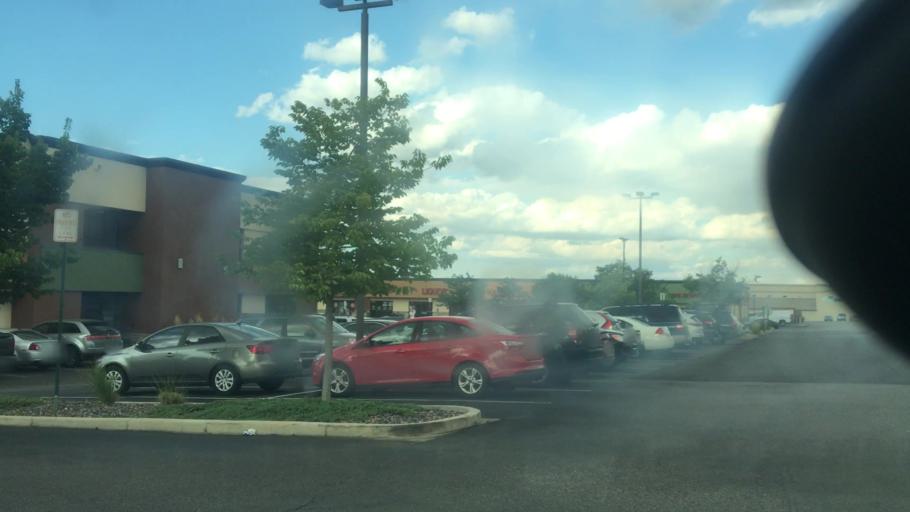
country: US
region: Colorado
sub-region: Arapahoe County
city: Centennial
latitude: 39.5941
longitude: -104.8784
